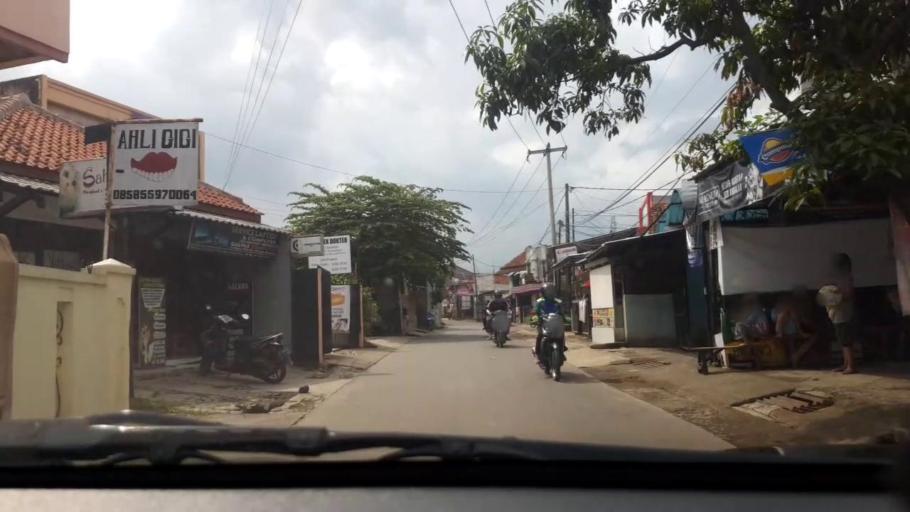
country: ID
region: West Java
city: Cileunyi
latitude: -6.9407
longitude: 107.7215
